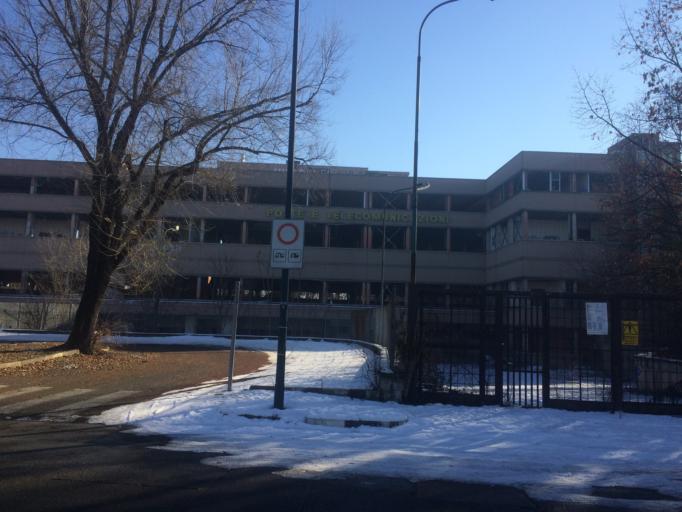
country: IT
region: Piedmont
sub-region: Provincia di Torino
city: Turin
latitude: 45.0858
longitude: 7.7097
